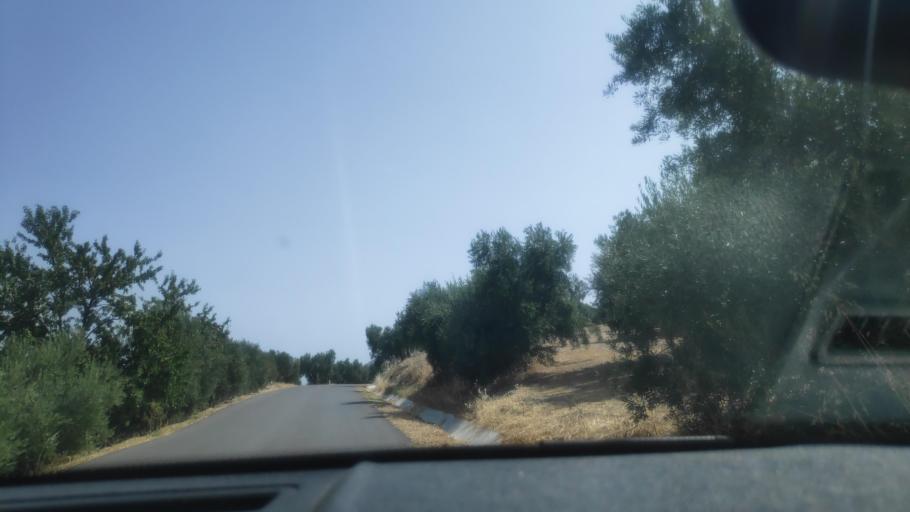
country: ES
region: Andalusia
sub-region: Provincia de Jaen
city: Jimena
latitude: 37.7919
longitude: -3.4520
